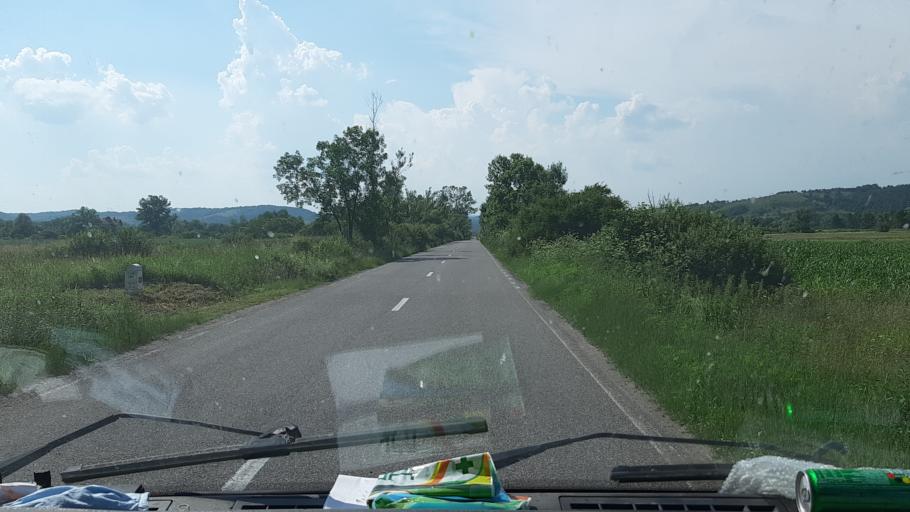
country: RO
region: Caras-Severin
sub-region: Comuna Ezeris
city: Ezeris
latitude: 45.3995
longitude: 21.9128
